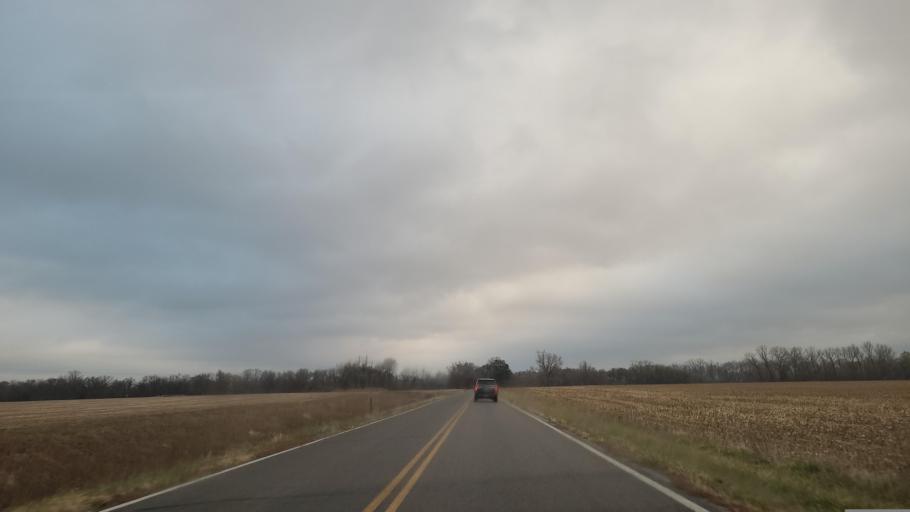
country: US
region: Kansas
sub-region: Douglas County
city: Lawrence
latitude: 38.9595
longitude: -95.2003
